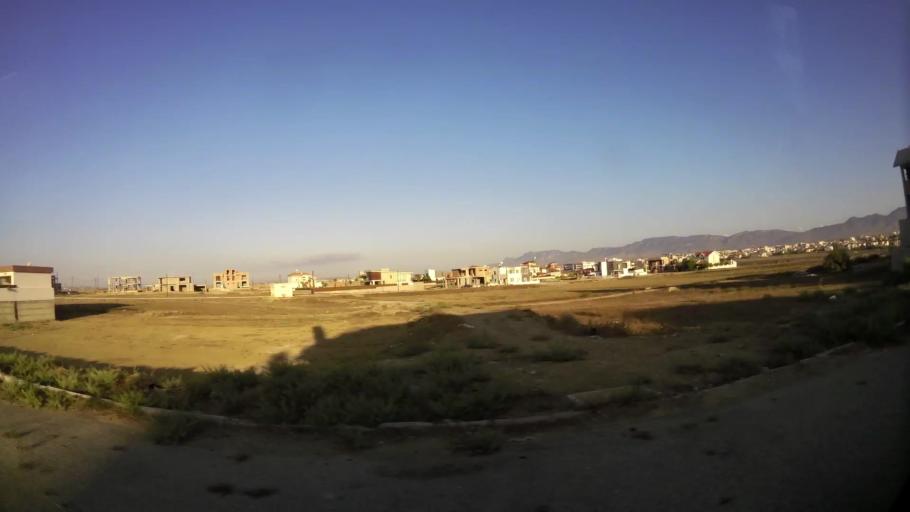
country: CY
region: Lefkosia
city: Nicosia
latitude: 35.1938
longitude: 33.3159
